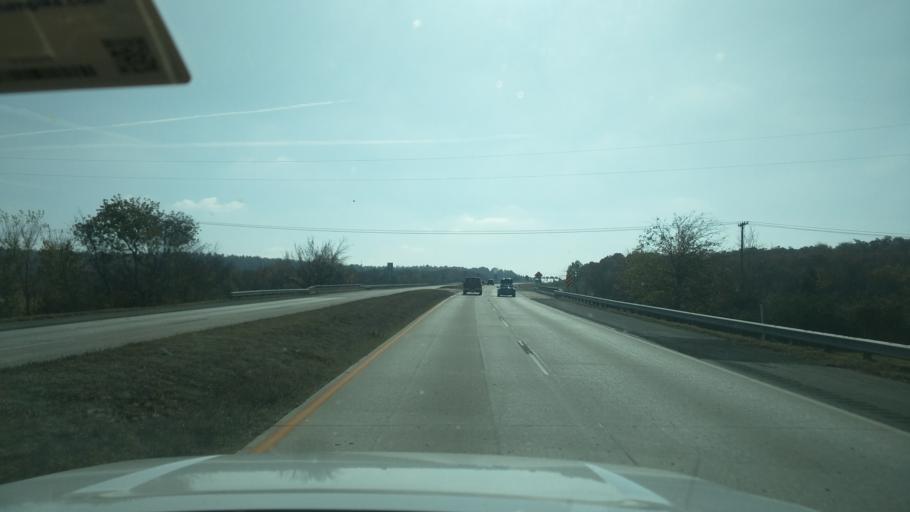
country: US
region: Oklahoma
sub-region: Muskogee County
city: Muskogee
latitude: 35.6688
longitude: -95.3087
